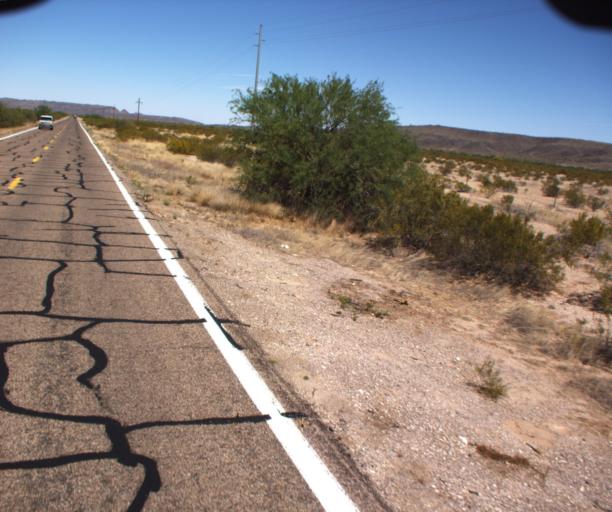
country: US
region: Arizona
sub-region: Pima County
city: Ajo
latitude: 32.4723
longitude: -112.8765
